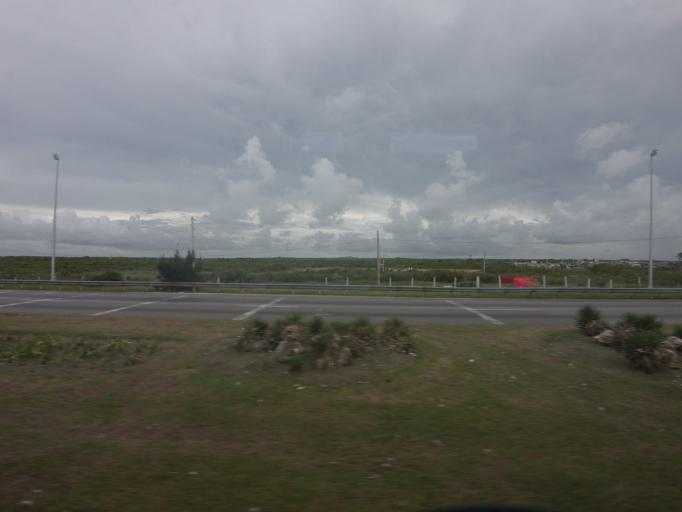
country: CU
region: Matanzas
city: Varadero
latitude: 23.1251
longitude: -81.3435
